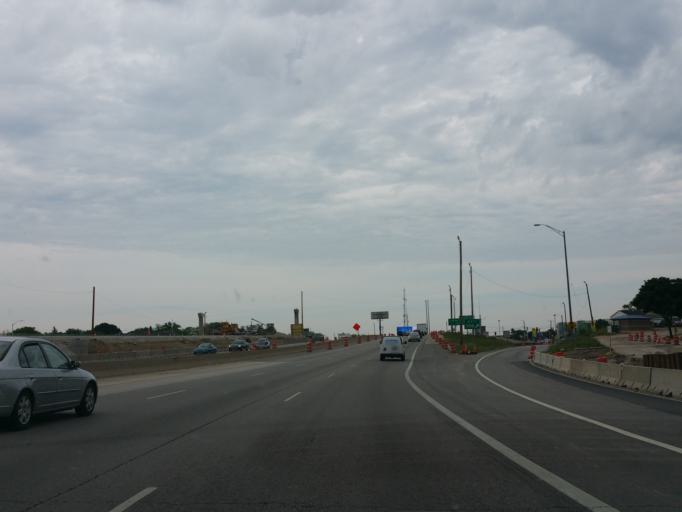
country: US
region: Wisconsin
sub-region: Milwaukee County
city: West Allis
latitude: 43.0279
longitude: -88.0205
